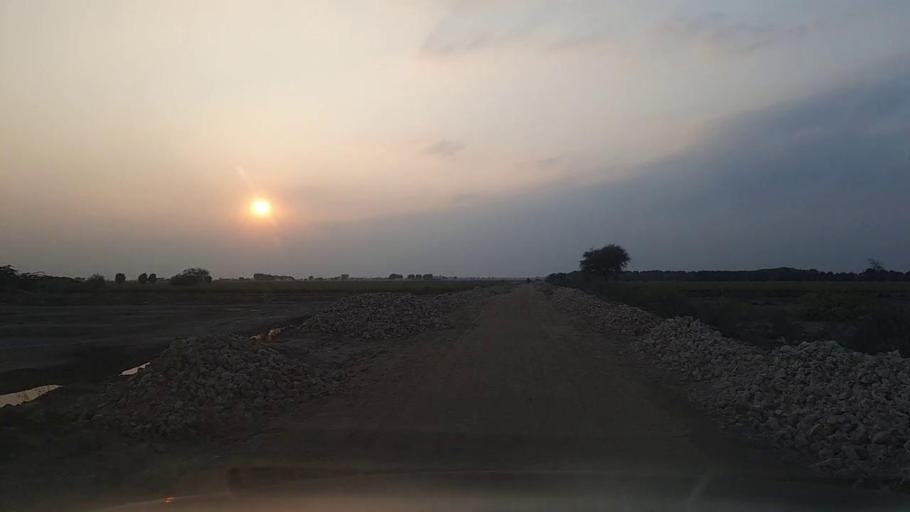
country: PK
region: Sindh
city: Jati
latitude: 24.5296
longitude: 68.4065
